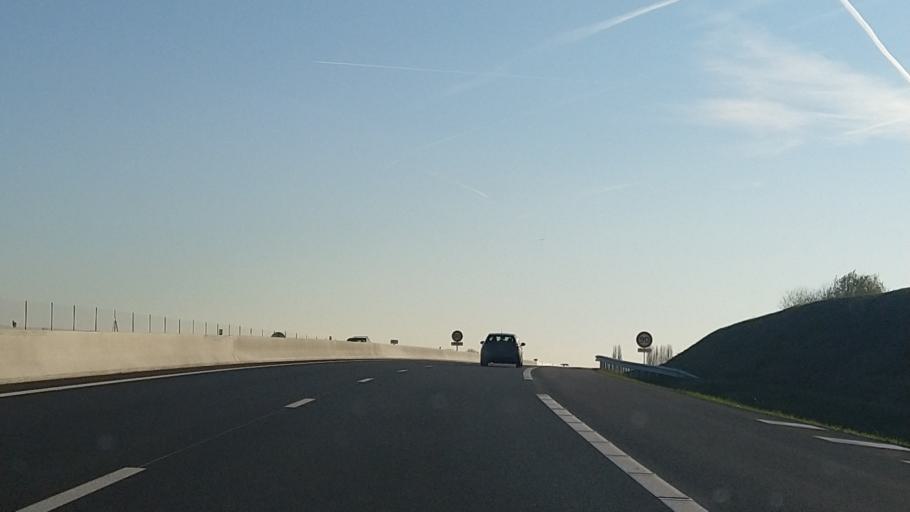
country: FR
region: Ile-de-France
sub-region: Departement du Val-d'Oise
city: Montsoult
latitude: 49.0764
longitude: 2.3325
